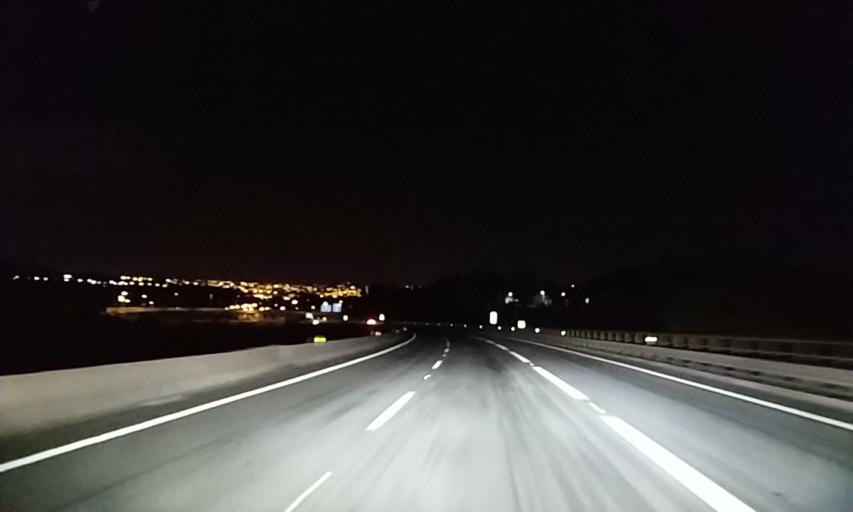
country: PT
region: Porto
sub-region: Vila Nova de Gaia
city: Perozinho
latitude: 41.0796
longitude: -8.5760
